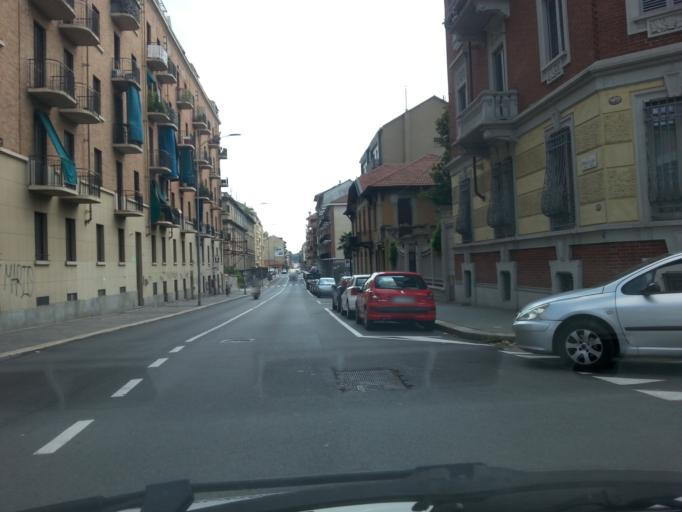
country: IT
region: Piedmont
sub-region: Provincia di Torino
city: Turin
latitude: 45.0889
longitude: 7.6832
